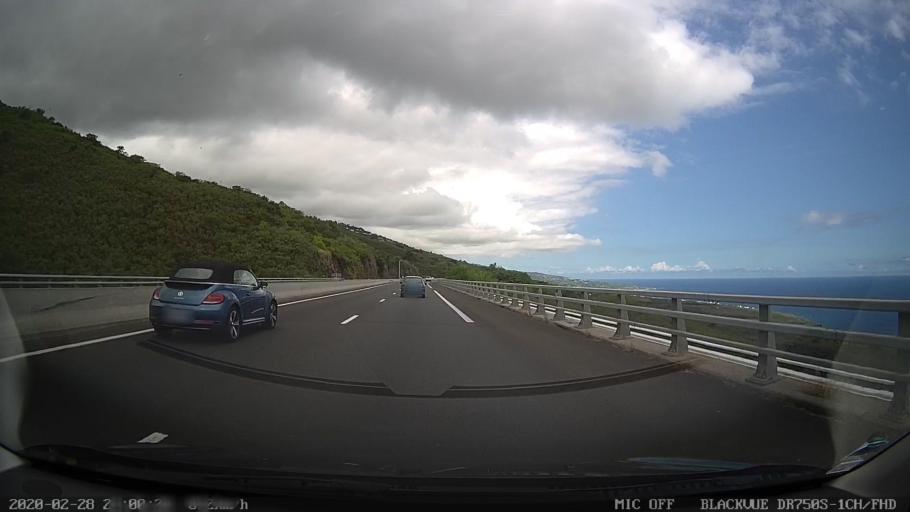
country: RE
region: Reunion
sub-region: Reunion
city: Trois-Bassins
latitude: -21.1185
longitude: 55.2772
